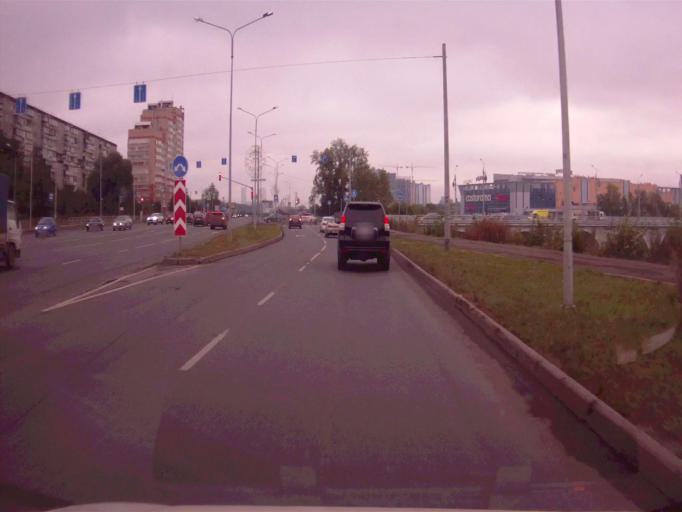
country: RU
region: Chelyabinsk
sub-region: Gorod Chelyabinsk
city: Chelyabinsk
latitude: 55.1728
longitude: 61.3495
